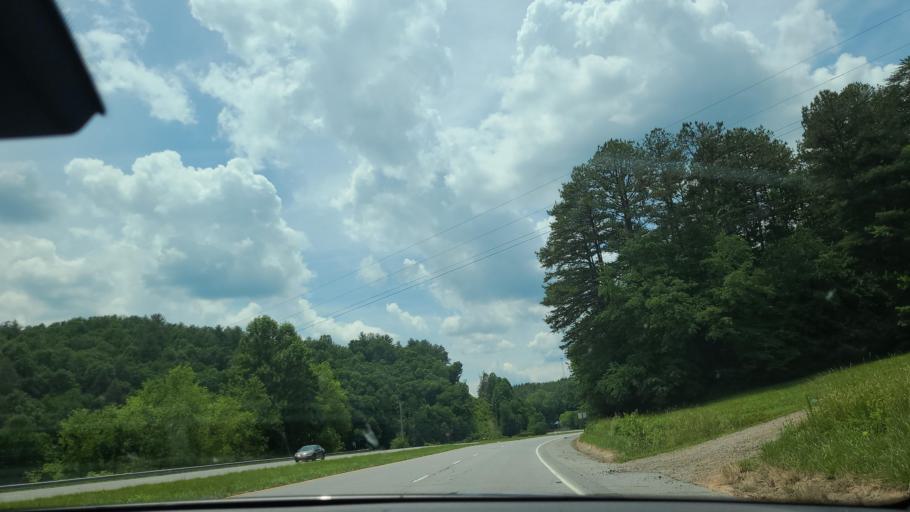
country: US
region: Georgia
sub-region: Fannin County
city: McCaysville
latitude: 35.0243
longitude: -84.2213
